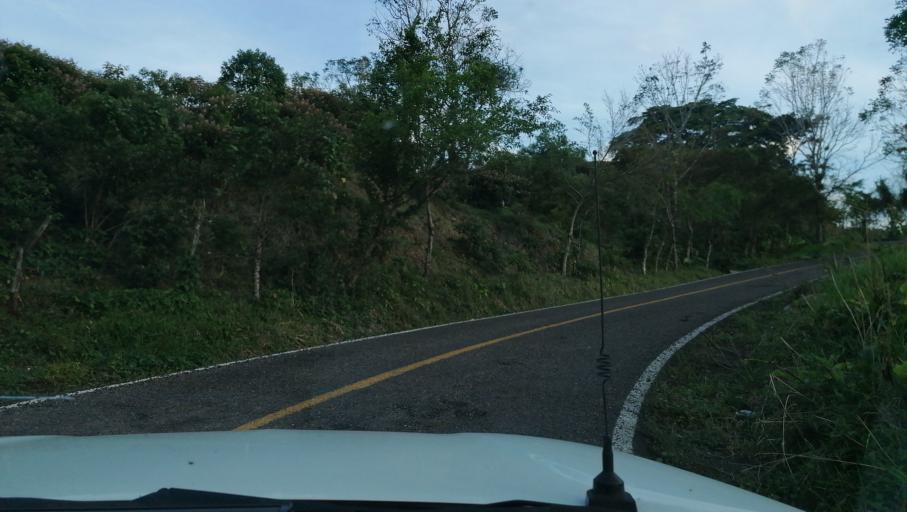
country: MX
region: Chiapas
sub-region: Juarez
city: El Triunfo 1ra. Seccion (Cardona)
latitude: 17.5018
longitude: -93.2446
